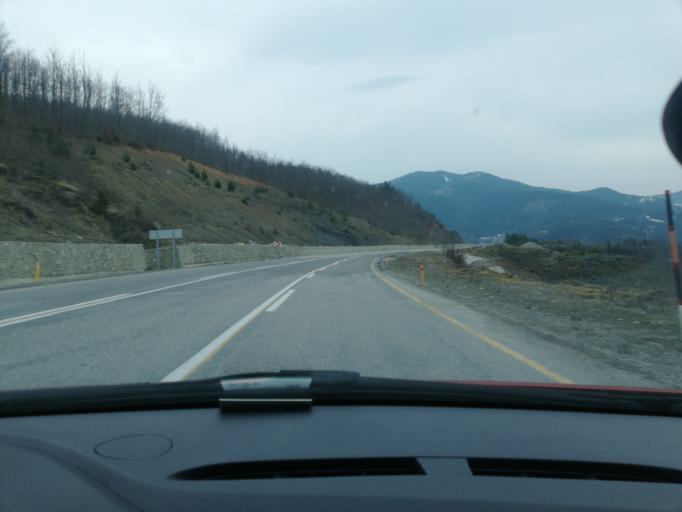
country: TR
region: Kastamonu
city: Kure
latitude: 41.8523
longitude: 33.7125
